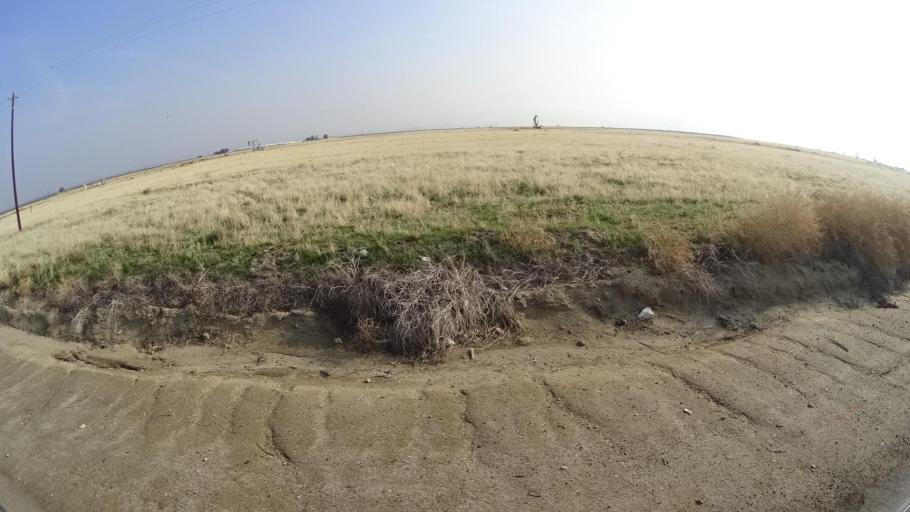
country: US
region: California
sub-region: Kern County
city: Lebec
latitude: 34.9884
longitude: -118.9087
